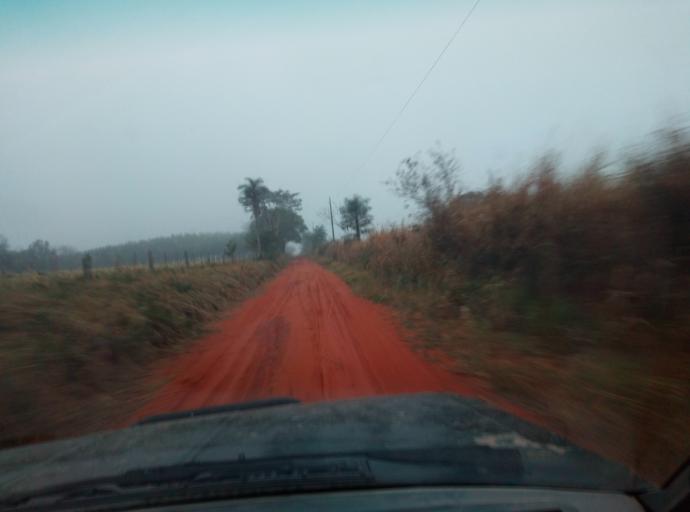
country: PY
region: Caaguazu
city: Doctor Cecilio Baez
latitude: -25.1556
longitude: -56.2842
